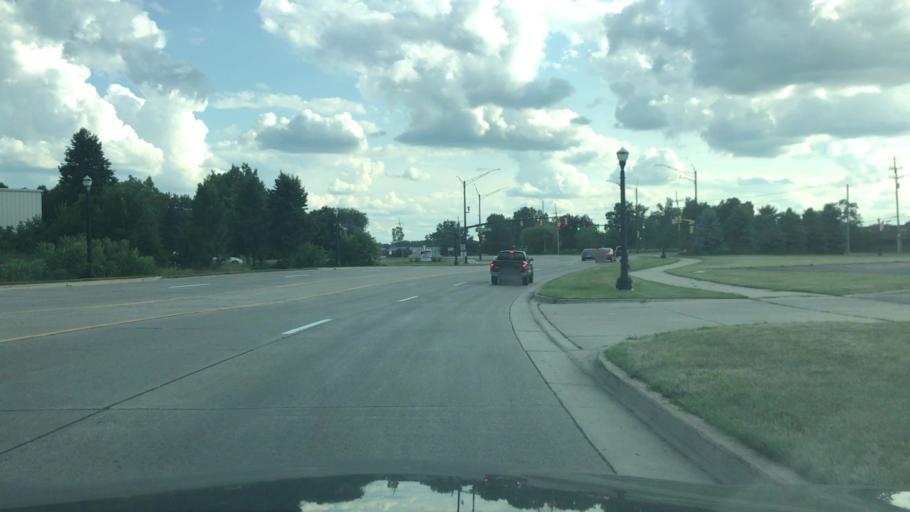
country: US
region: Michigan
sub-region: Oakland County
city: Wixom
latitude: 42.5226
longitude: -83.5363
